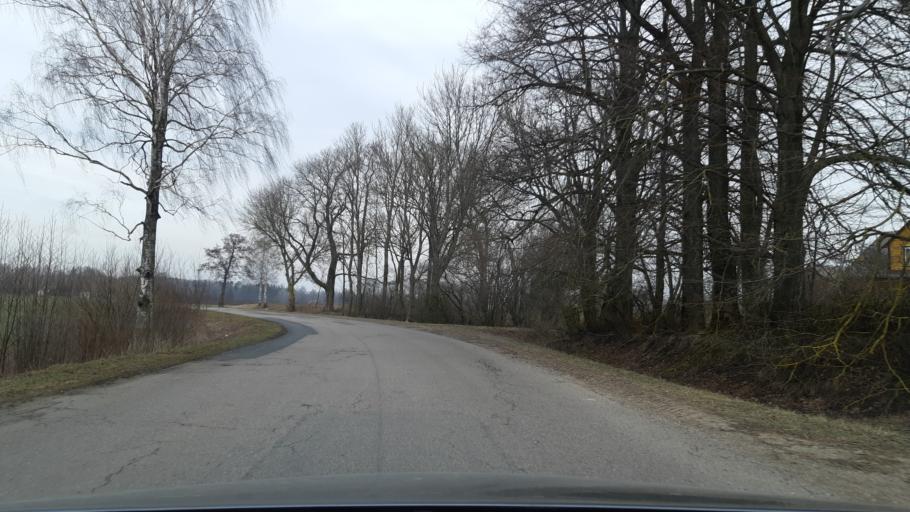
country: LT
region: Marijampoles apskritis
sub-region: Marijampole Municipality
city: Marijampole
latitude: 54.7232
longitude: 23.3369
